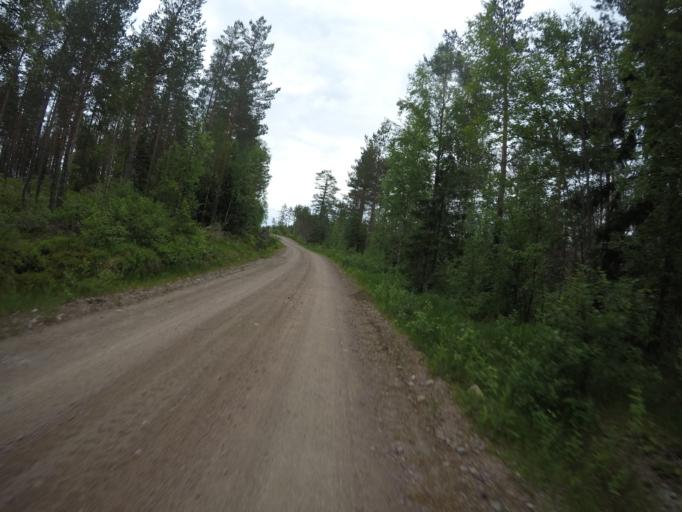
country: SE
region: Dalarna
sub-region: Ludvika Kommun
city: Abborrberget
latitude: 60.0862
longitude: 14.5512
